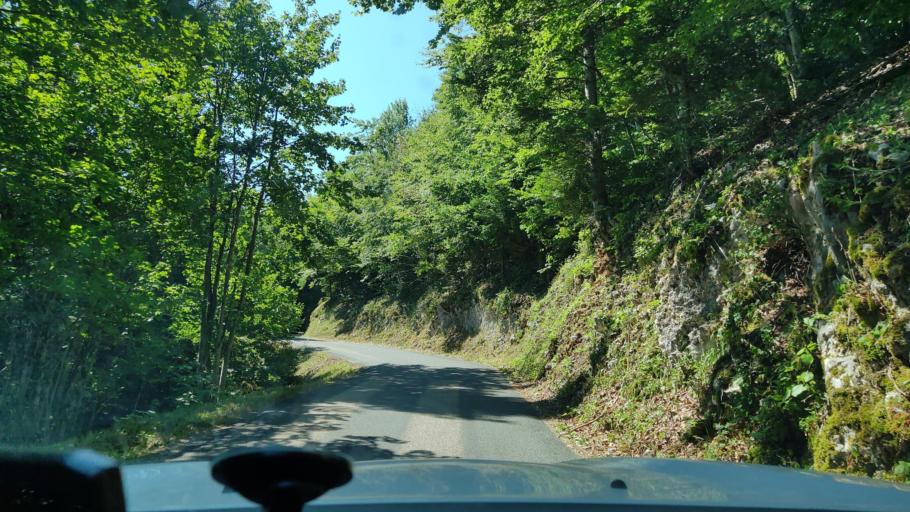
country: FR
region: Rhone-Alpes
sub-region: Departement de la Savoie
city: Le Bourget-du-Lac
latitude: 45.6454
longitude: 5.8259
